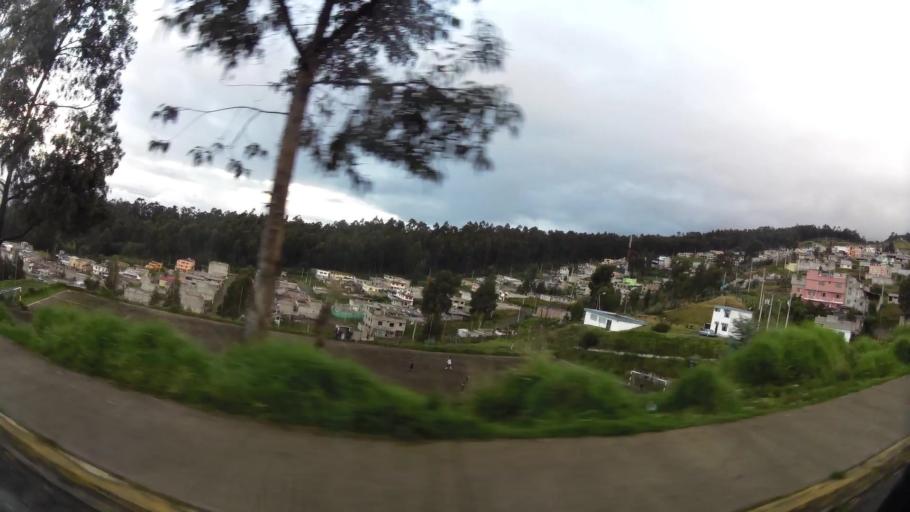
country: EC
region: Pichincha
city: Quito
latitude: -0.1019
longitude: -78.5229
